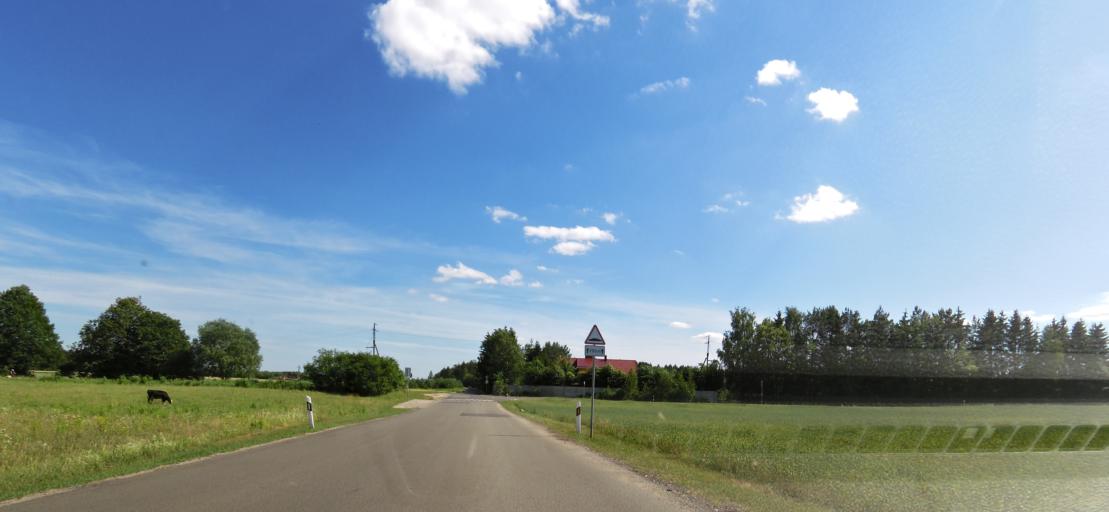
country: LT
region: Vilnius County
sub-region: Vilnius
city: Fabijoniskes
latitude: 54.8070
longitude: 25.3268
